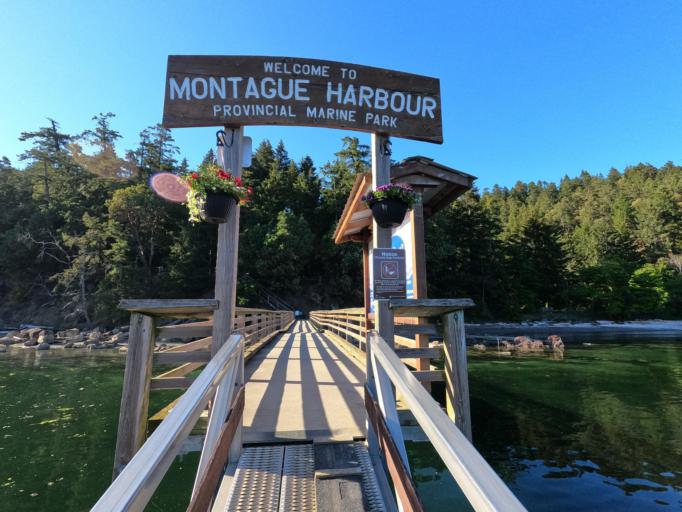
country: CA
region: British Columbia
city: North Saanich
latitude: 48.8970
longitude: -123.4026
